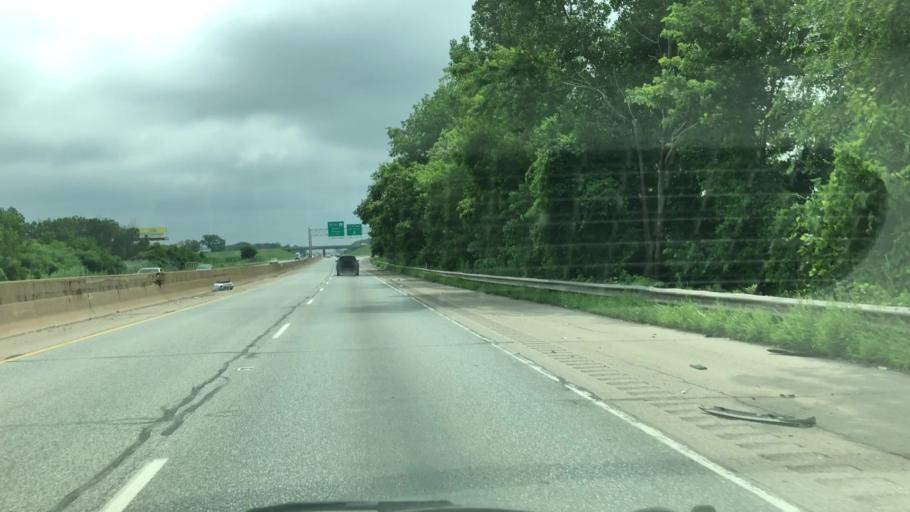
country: US
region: Indiana
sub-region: Lake County
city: Highland
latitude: 41.5930
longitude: -87.4329
